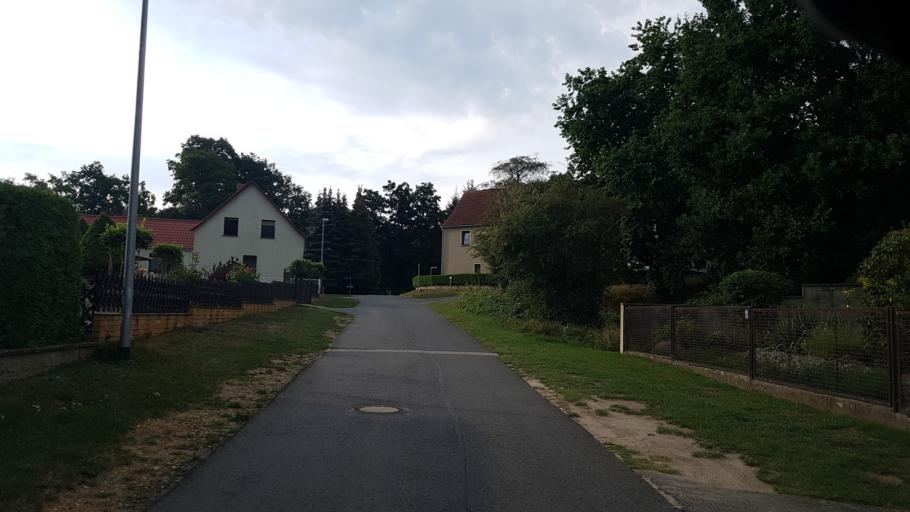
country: DE
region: Brandenburg
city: Hirschfeld
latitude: 51.3838
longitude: 13.6197
